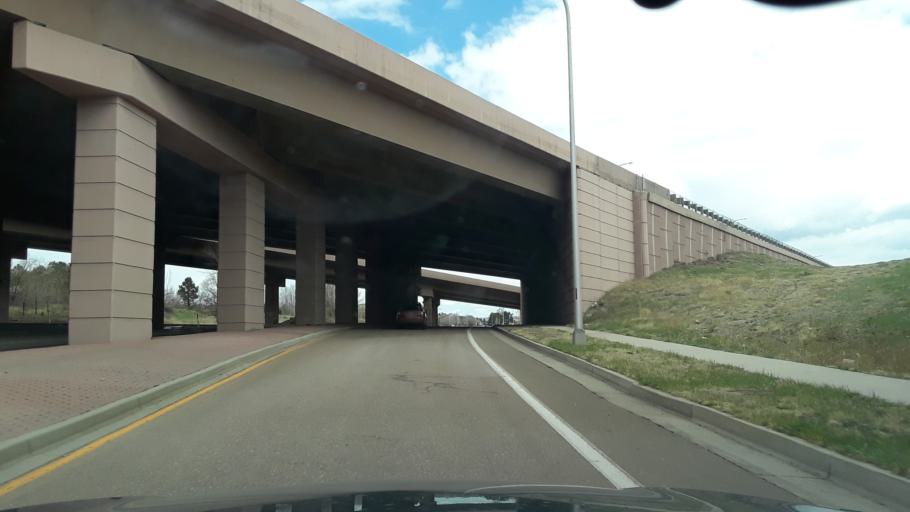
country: US
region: Colorado
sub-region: El Paso County
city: Colorado Springs
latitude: 38.9104
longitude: -104.8230
